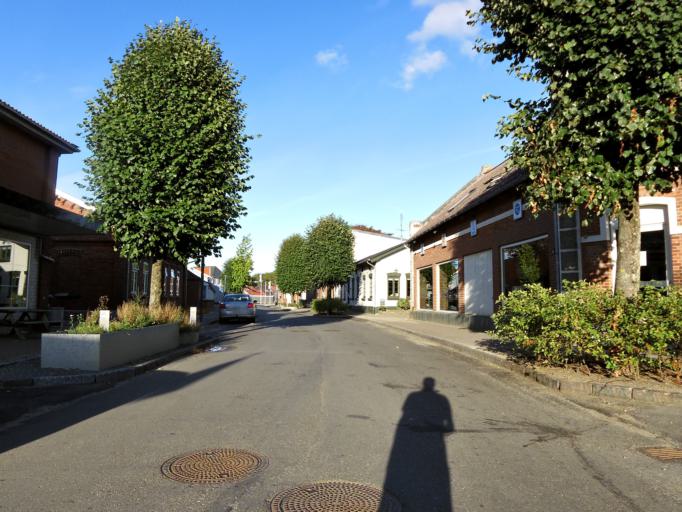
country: DK
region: South Denmark
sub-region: Tonder Kommune
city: Sherrebek
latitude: 55.0583
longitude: 8.8274
